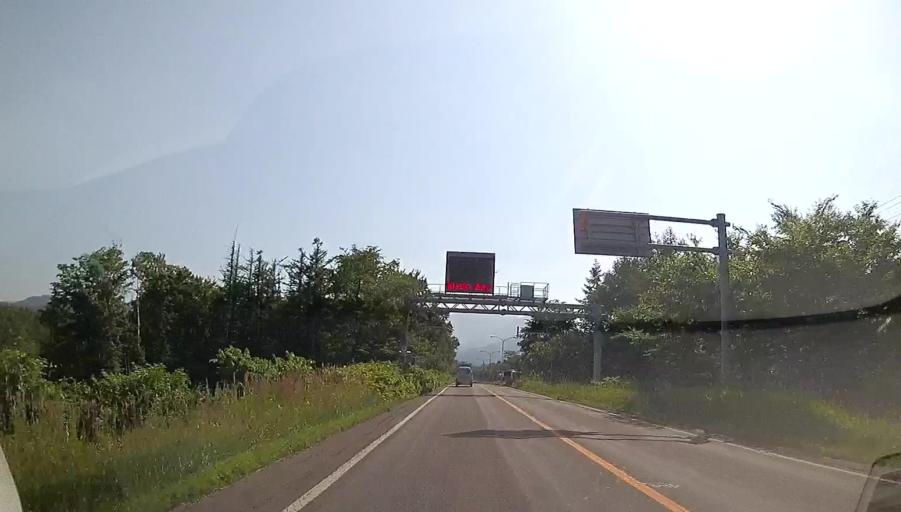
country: JP
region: Hokkaido
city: Otofuke
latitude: 42.9921
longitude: 142.8468
